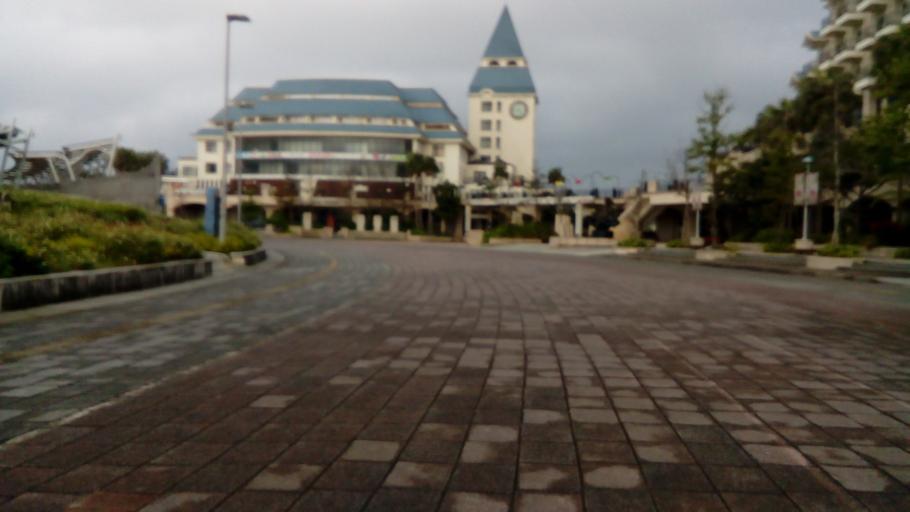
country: TW
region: Taipei
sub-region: Taipei
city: Banqiao
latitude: 25.1819
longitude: 121.4153
